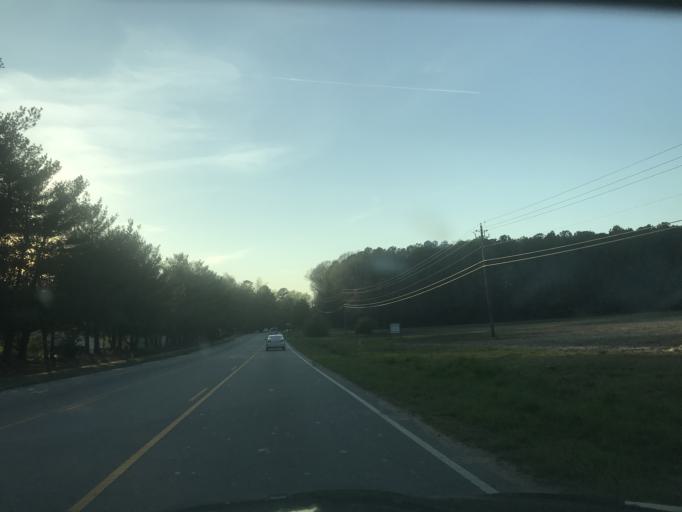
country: US
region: North Carolina
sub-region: Wake County
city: Knightdale
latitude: 35.7578
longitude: -78.5464
